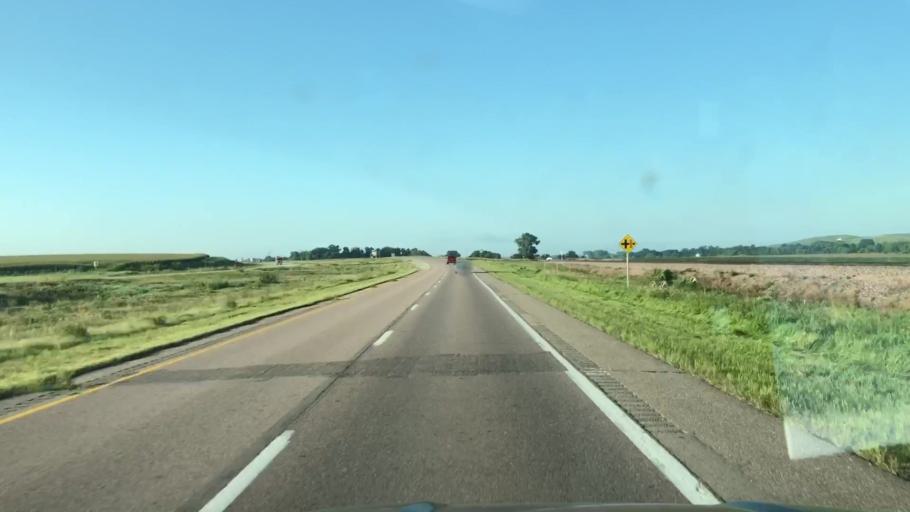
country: US
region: Iowa
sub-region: O'Brien County
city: Sheldon
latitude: 43.1439
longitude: -95.8799
